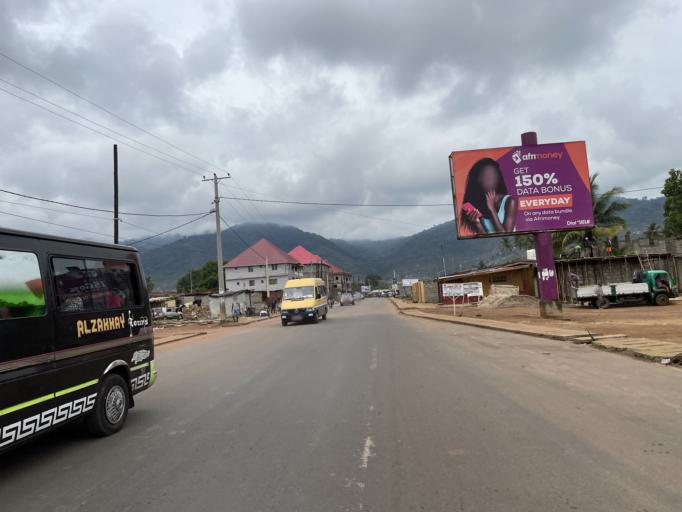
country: SL
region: Western Area
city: Hastings
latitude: 8.3895
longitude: -13.1474
